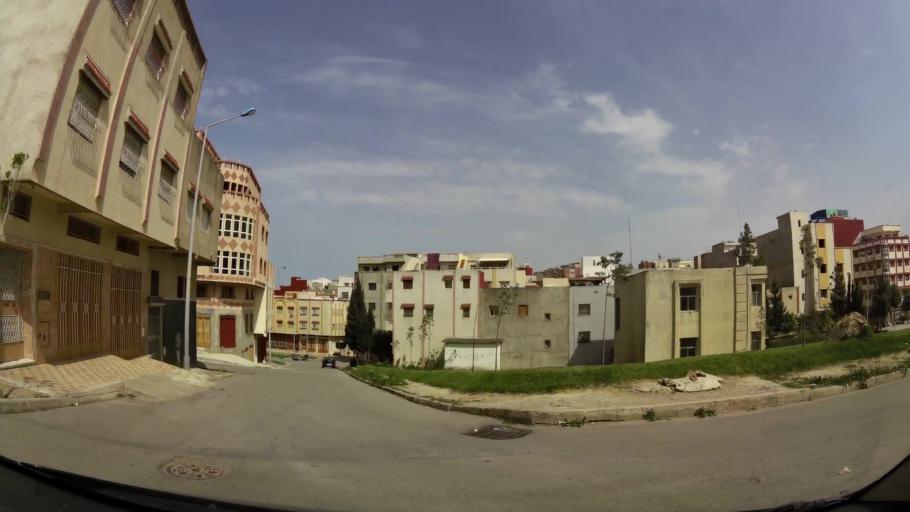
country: MA
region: Tanger-Tetouan
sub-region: Tanger-Assilah
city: Tangier
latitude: 35.7415
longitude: -5.8330
